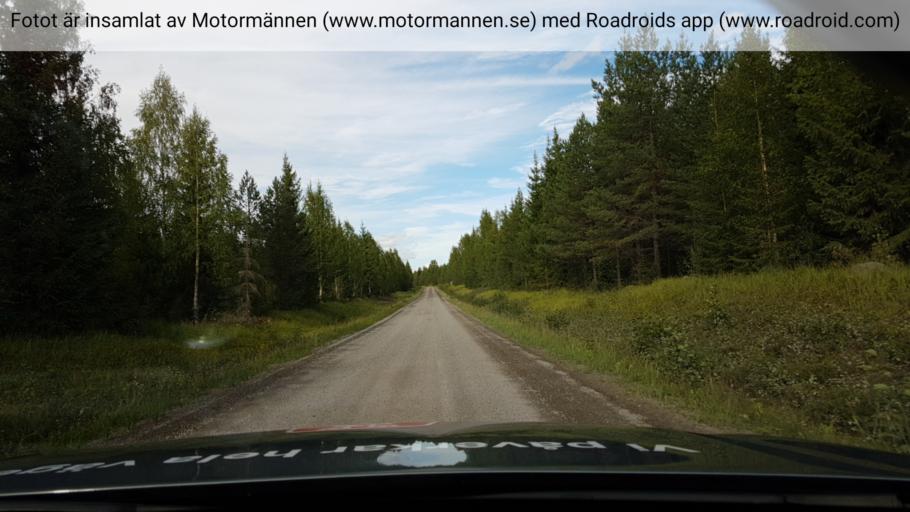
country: SE
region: Jaemtland
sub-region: Braecke Kommun
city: Braecke
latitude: 63.2314
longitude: 15.3559
